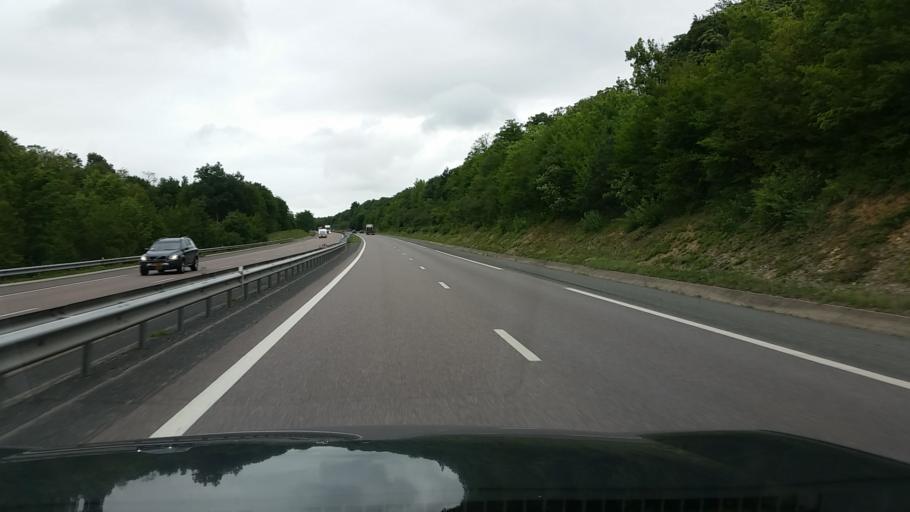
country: FR
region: Lorraine
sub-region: Departement de Meurthe-et-Moselle
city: Colombey-les-Belles
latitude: 48.4862
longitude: 5.9007
